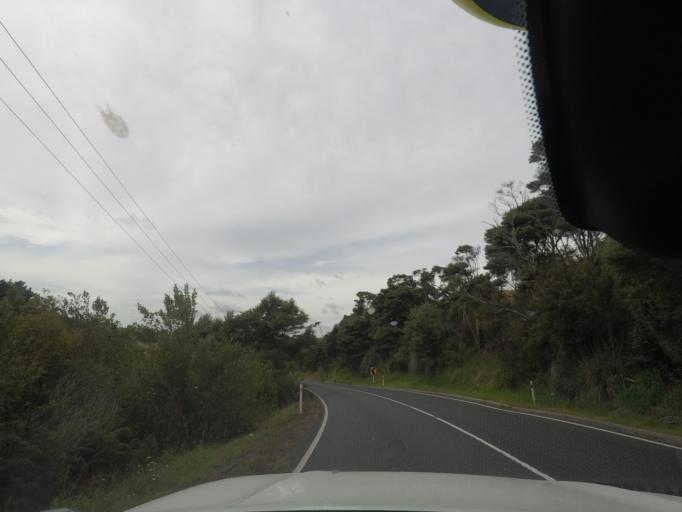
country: NZ
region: Auckland
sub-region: Auckland
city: Parakai
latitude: -36.5806
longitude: 174.3273
